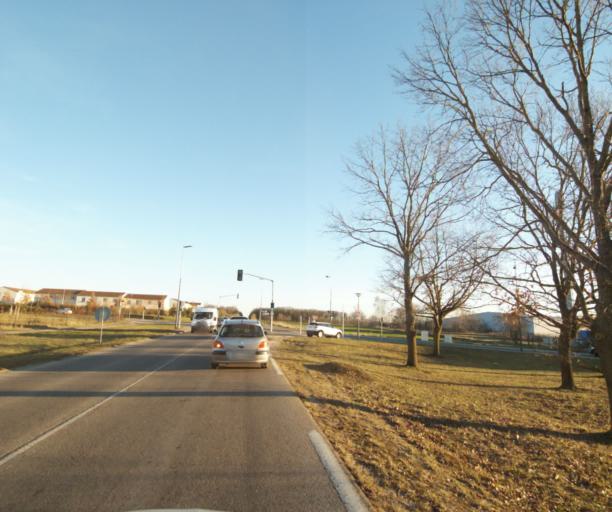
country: FR
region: Lorraine
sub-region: Departement de Meurthe-et-Moselle
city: Tomblaine
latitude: 48.6762
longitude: 6.2270
